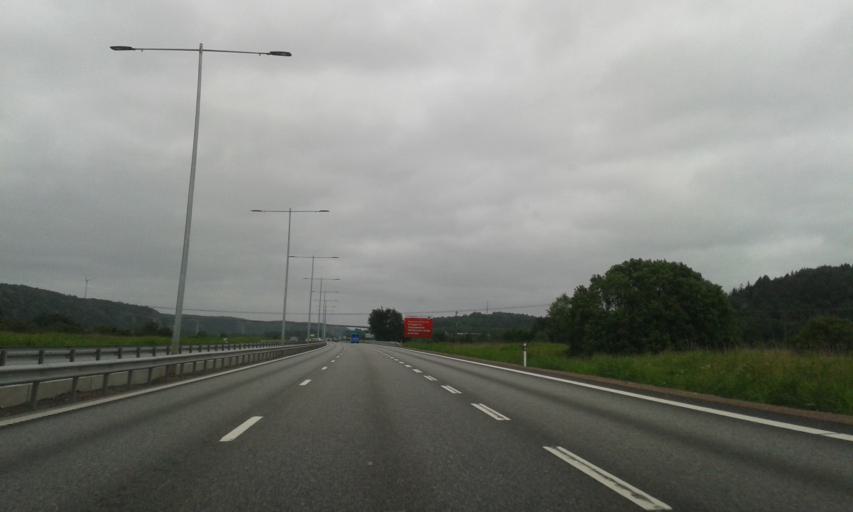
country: SE
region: Vaestra Goetaland
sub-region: Ale Kommun
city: Surte
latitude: 57.8218
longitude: 12.0041
